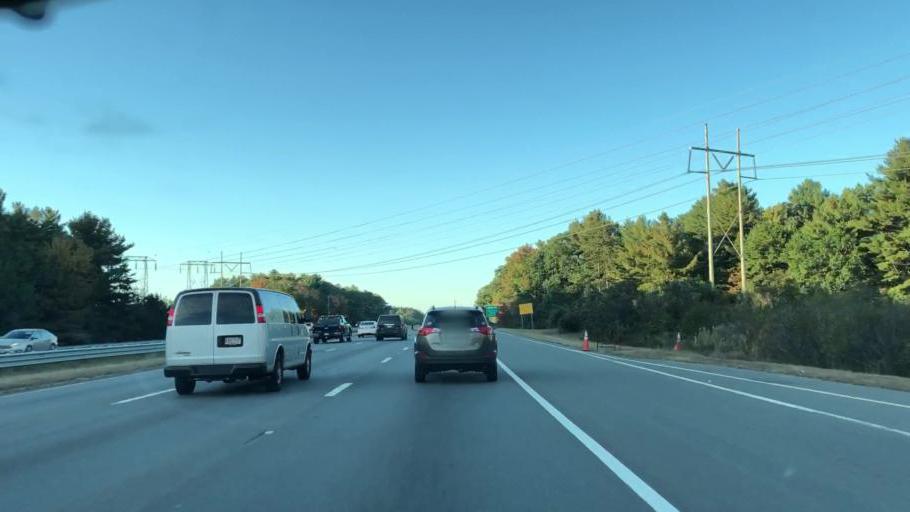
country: US
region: Massachusetts
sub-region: Middlesex County
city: Wilmington
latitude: 42.6024
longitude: -71.1710
